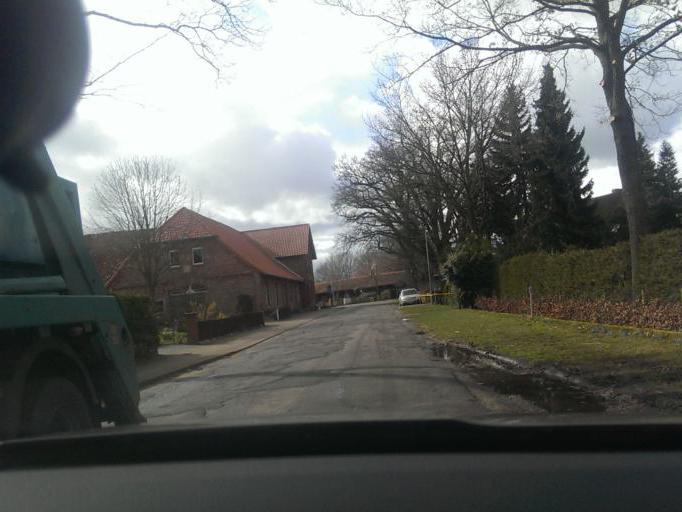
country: DE
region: Lower Saxony
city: Elze
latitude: 52.5634
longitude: 9.7686
